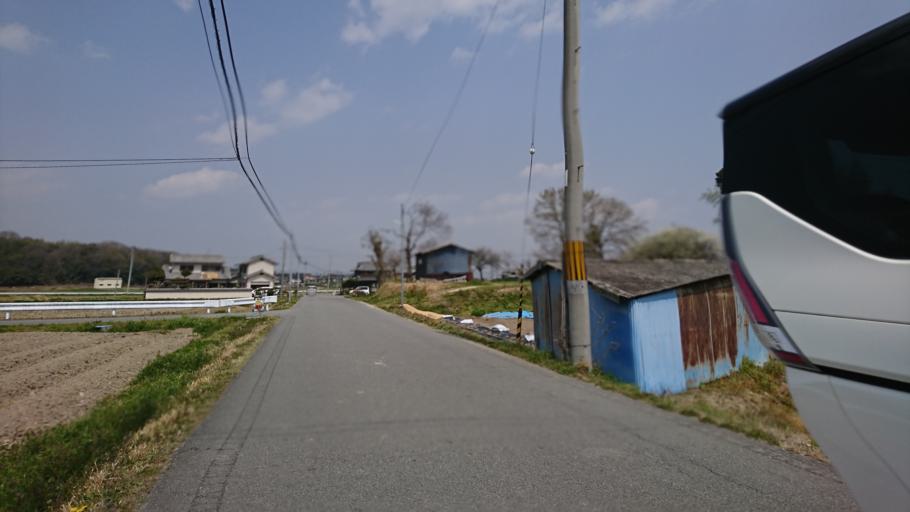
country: JP
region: Hyogo
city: Ono
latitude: 34.8337
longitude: 134.9053
